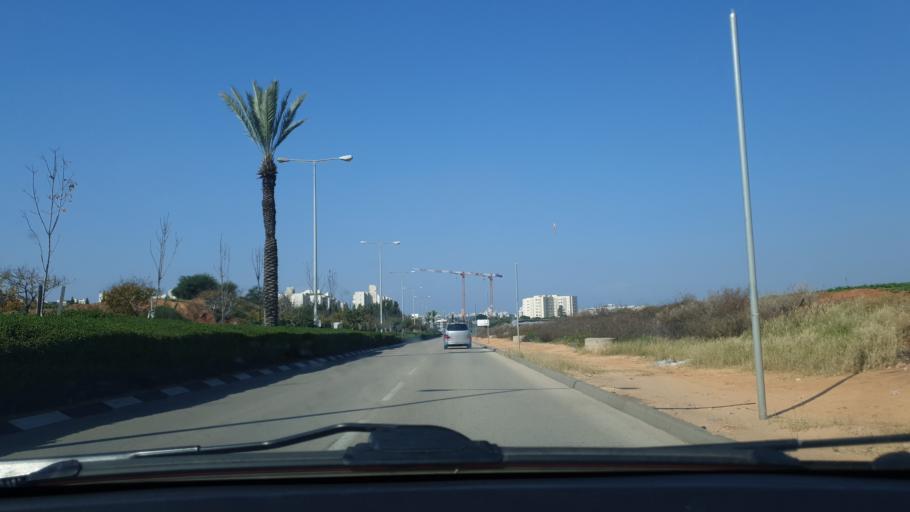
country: IL
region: Central District
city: Bet Dagan
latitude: 31.9720
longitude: 34.8222
